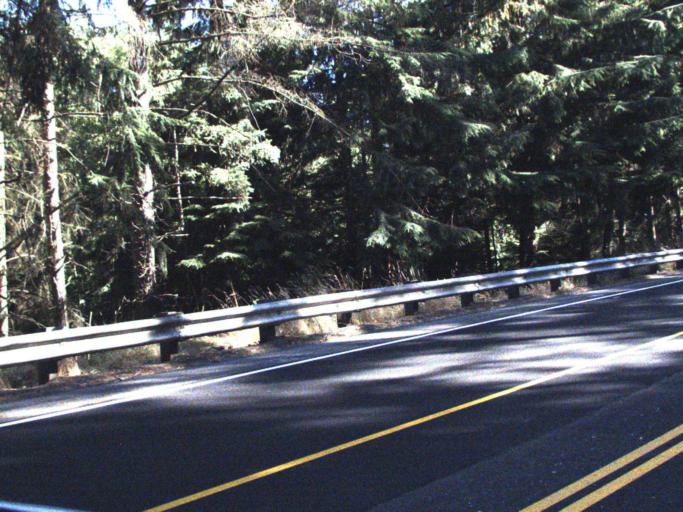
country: US
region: Washington
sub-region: Pierce County
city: Buckley
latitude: 47.1762
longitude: -122.0210
